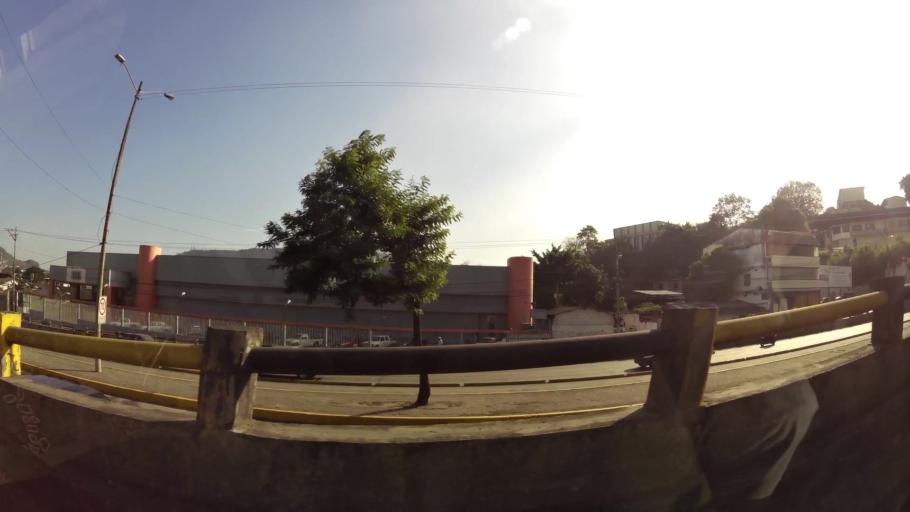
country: EC
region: Guayas
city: Guayaquil
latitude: -2.1500
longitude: -79.9323
